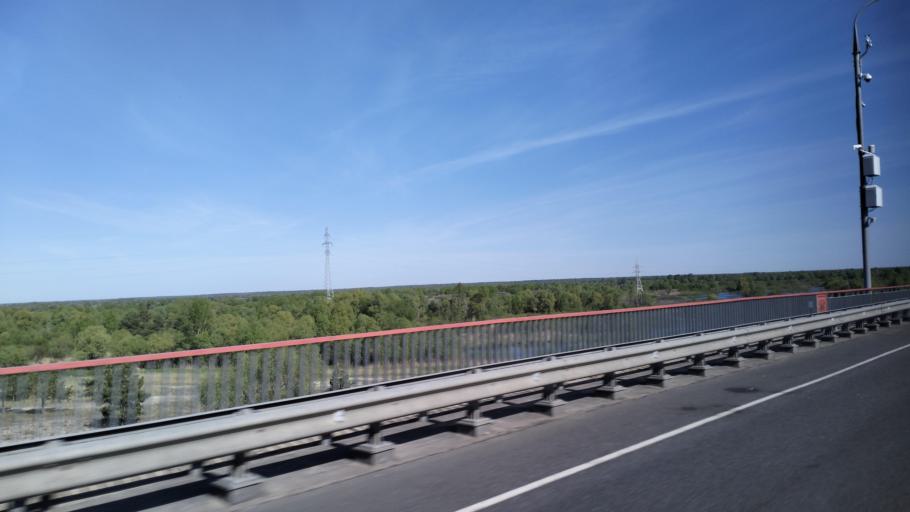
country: BY
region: Gomel
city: Turaw
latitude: 52.0804
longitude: 27.8262
